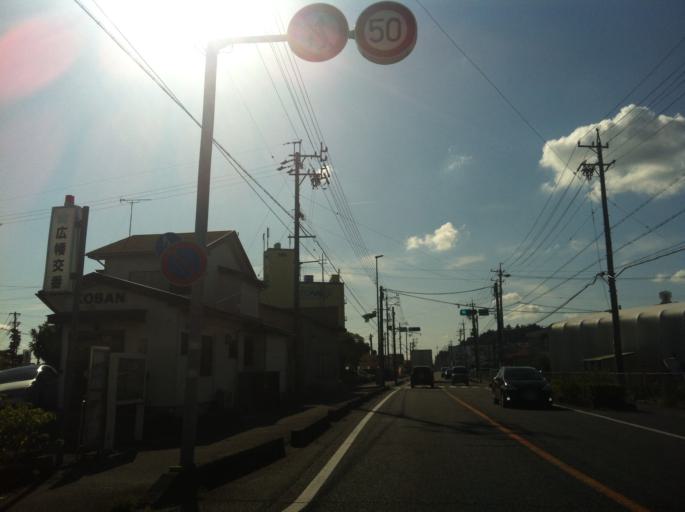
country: JP
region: Shizuoka
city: Fujieda
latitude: 34.8912
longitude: 138.2806
